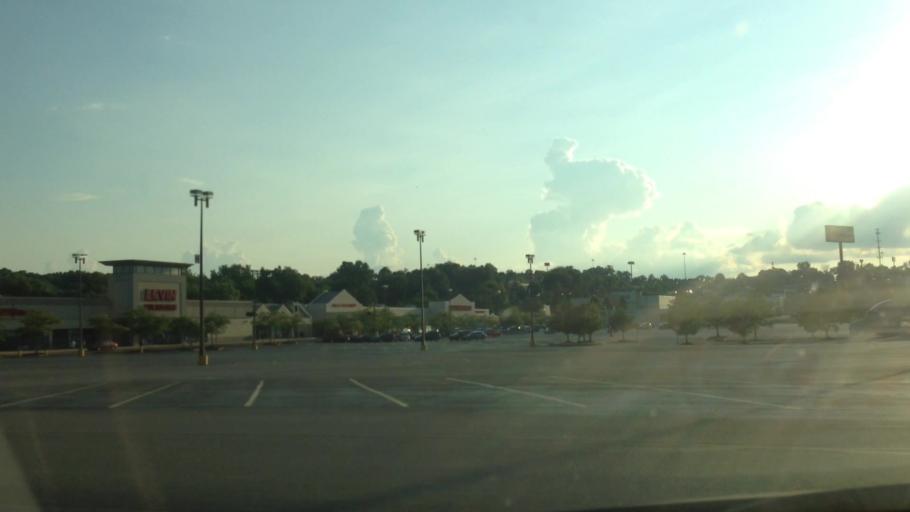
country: US
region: Ohio
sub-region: Summit County
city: Montrose-Ghent
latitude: 41.1326
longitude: -81.6435
